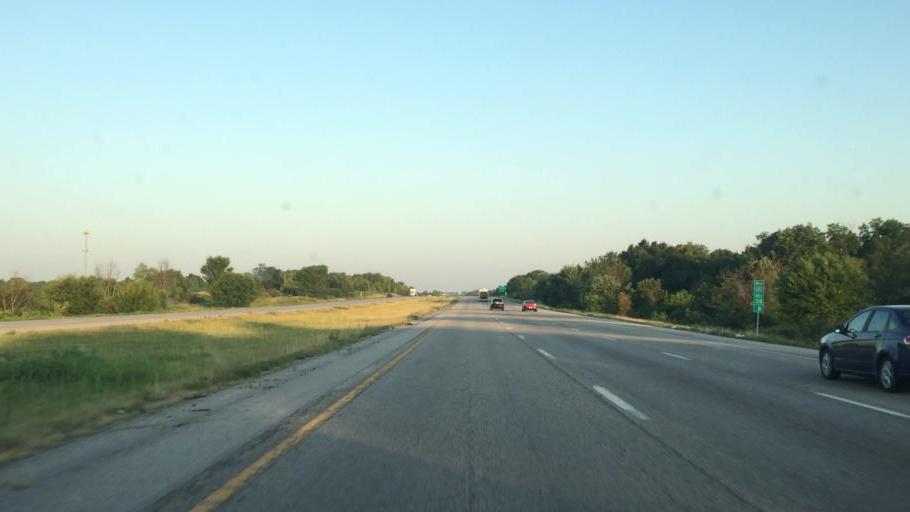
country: US
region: Missouri
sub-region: Clay County
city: Smithville
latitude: 39.3075
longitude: -94.6285
